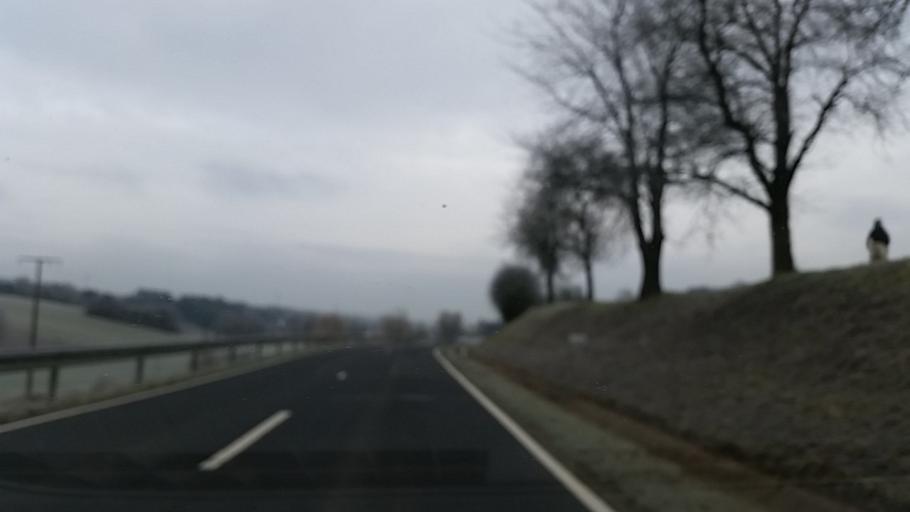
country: DE
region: Bavaria
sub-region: Regierungsbezirk Unterfranken
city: Thungen
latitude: 50.0190
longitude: 9.8837
